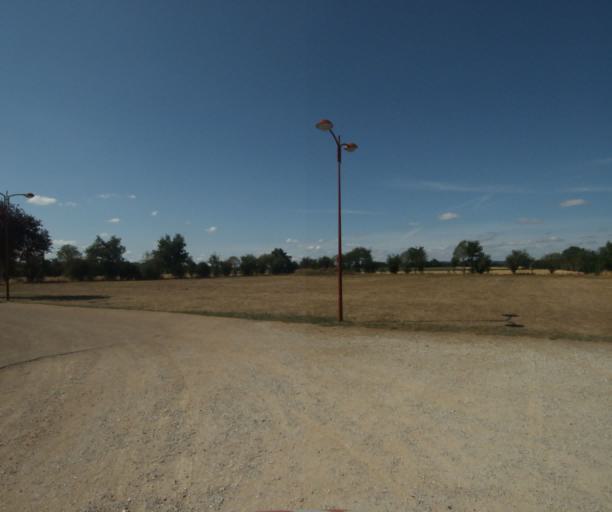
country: FR
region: Midi-Pyrenees
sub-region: Departement de la Haute-Garonne
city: Revel
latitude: 43.4902
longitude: 1.9812
